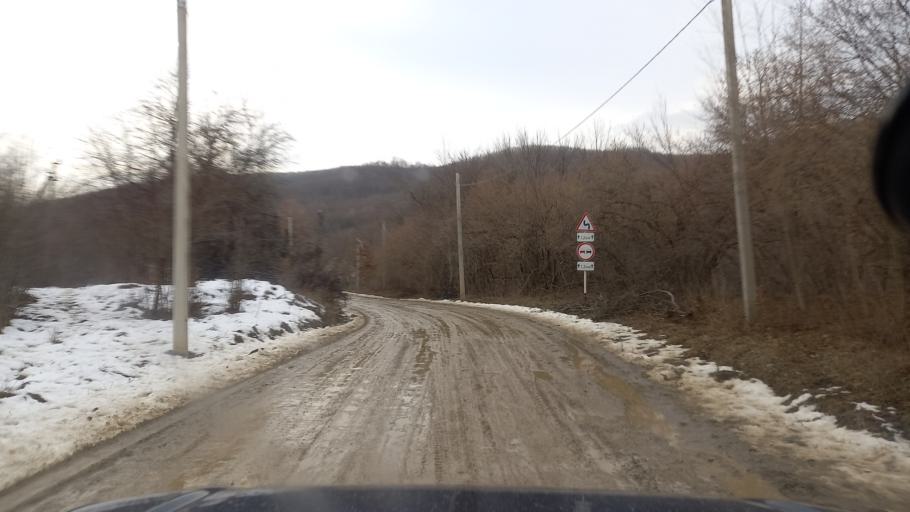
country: RU
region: Adygeya
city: Kamennomostskiy
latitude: 44.1414
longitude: 40.2800
